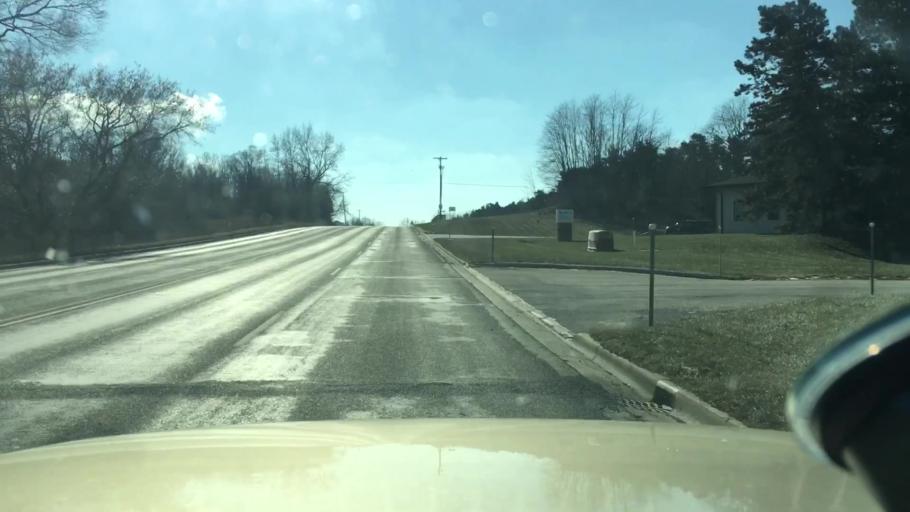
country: US
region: Michigan
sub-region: Jackson County
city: Jackson
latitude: 42.2854
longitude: -84.3844
